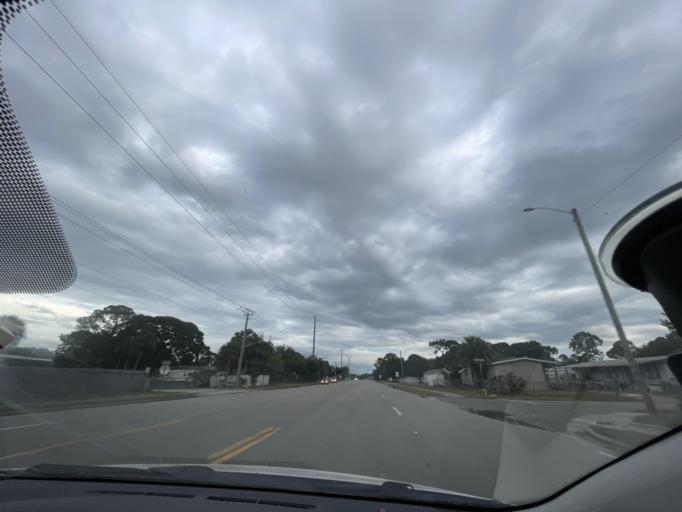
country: US
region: Florida
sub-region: Volusia County
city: Port Orange
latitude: 29.1105
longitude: -80.9934
